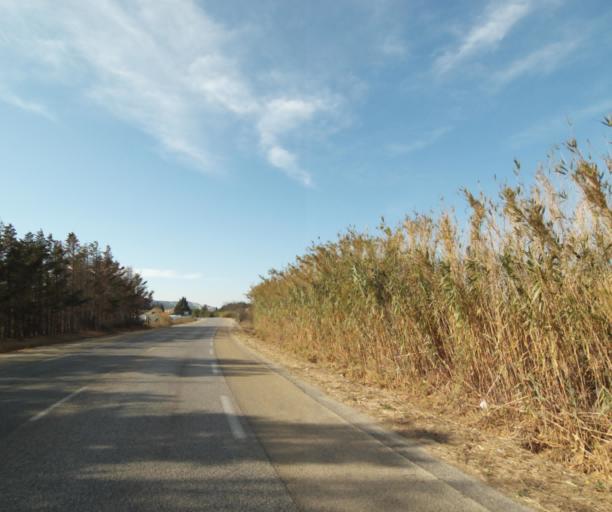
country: FR
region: Provence-Alpes-Cote d'Azur
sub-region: Departement des Bouches-du-Rhone
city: Chateauneuf-les-Martigues
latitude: 43.3804
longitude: 5.1861
